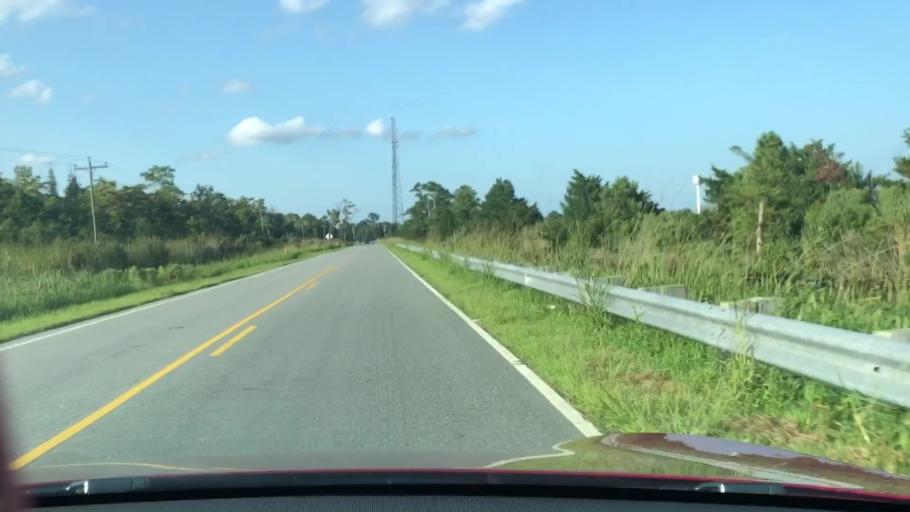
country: US
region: North Carolina
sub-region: Dare County
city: Wanchese
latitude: 35.7023
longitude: -75.7706
